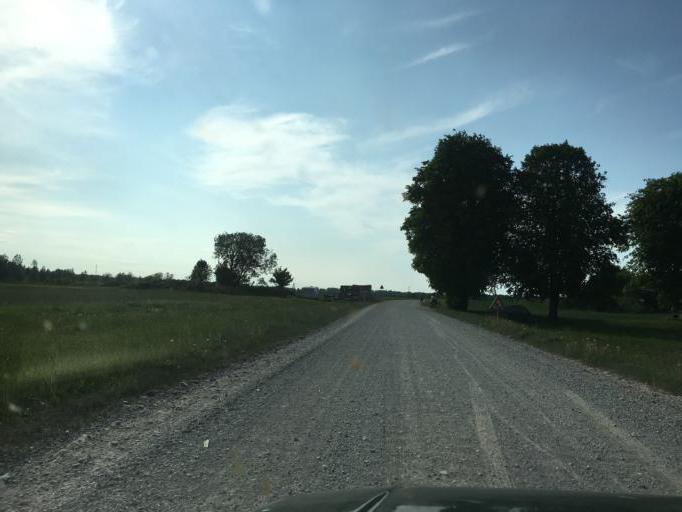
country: LV
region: Dundaga
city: Dundaga
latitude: 57.6217
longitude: 22.4123
